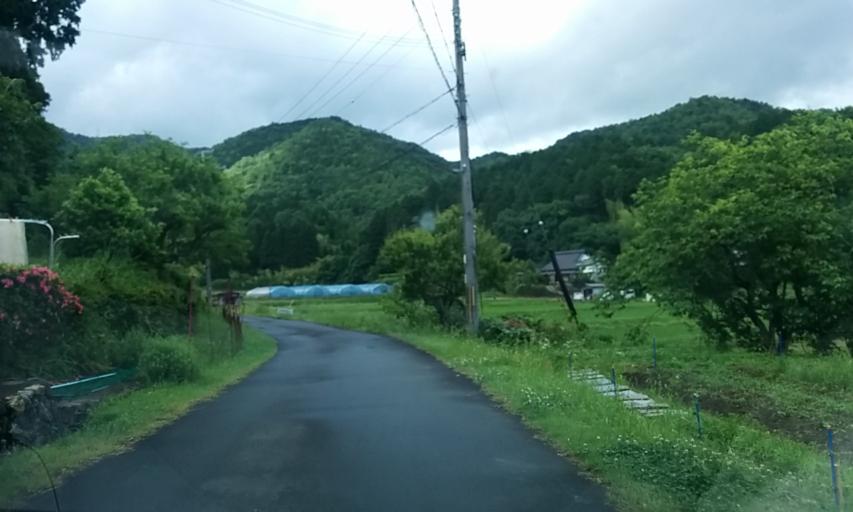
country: JP
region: Kyoto
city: Ayabe
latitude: 35.3888
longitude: 135.2385
